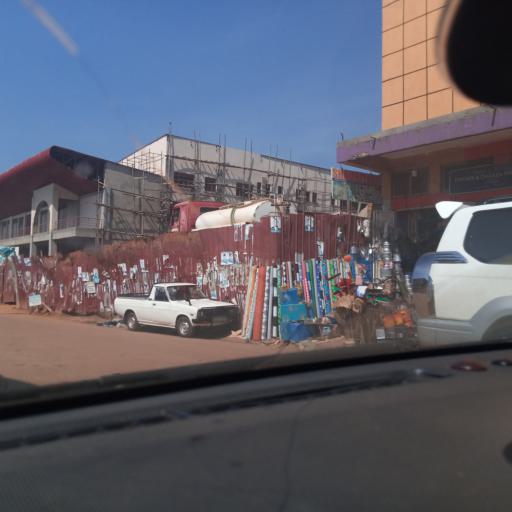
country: UG
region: Central Region
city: Masaka
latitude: -0.3457
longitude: 31.7388
